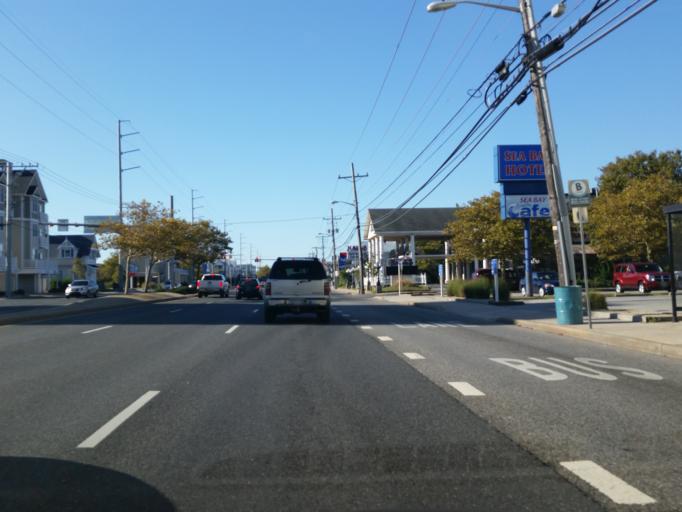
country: US
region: Maryland
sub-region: Worcester County
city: Ocean City
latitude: 38.3840
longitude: -75.0668
